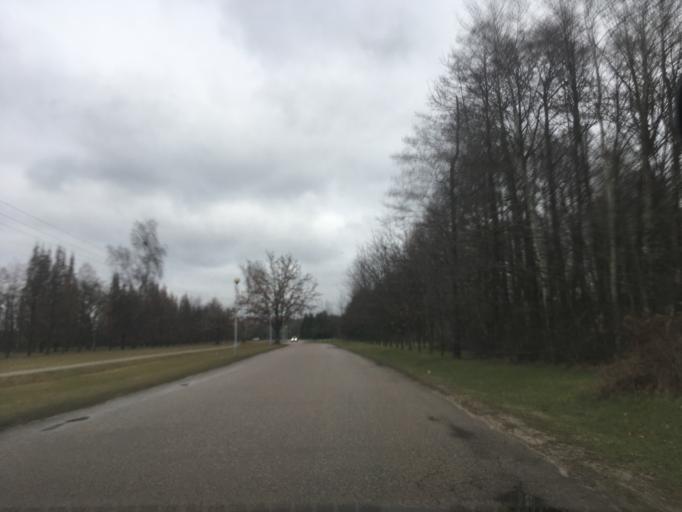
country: PL
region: Masovian Voivodeship
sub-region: Powiat piaseczynski
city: Lesznowola
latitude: 52.0578
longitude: 20.9058
